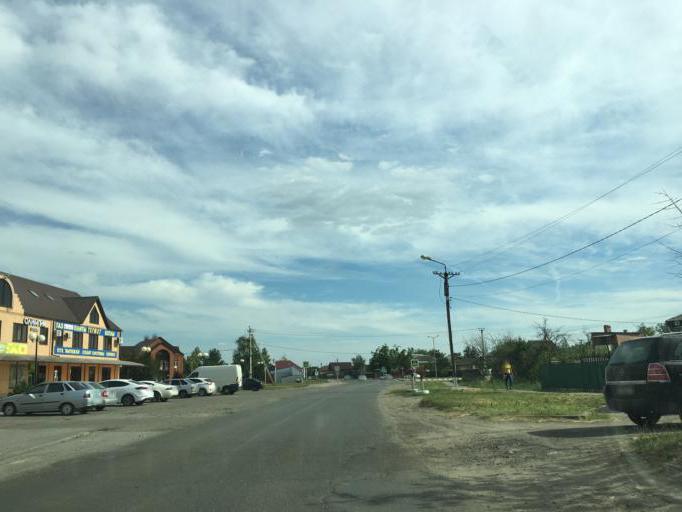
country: RU
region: Krasnodarskiy
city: Kushchevskaya
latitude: 46.5604
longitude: 39.6336
